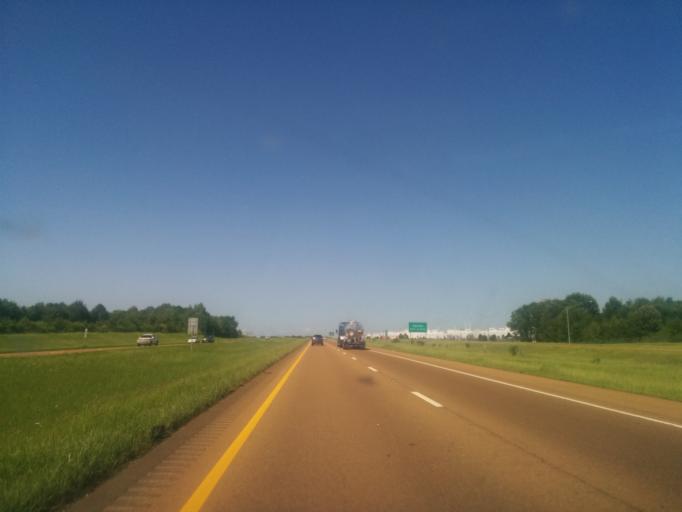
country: US
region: Mississippi
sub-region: Madison County
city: Canton
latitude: 32.5637
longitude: -90.0794
